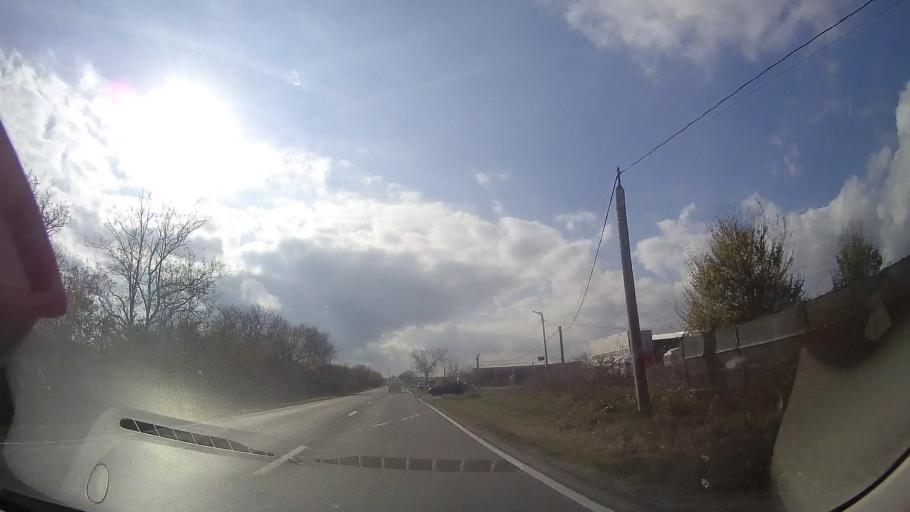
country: RO
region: Constanta
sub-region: Comuna Agigea
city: Agigea
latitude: 44.0827
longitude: 28.6055
